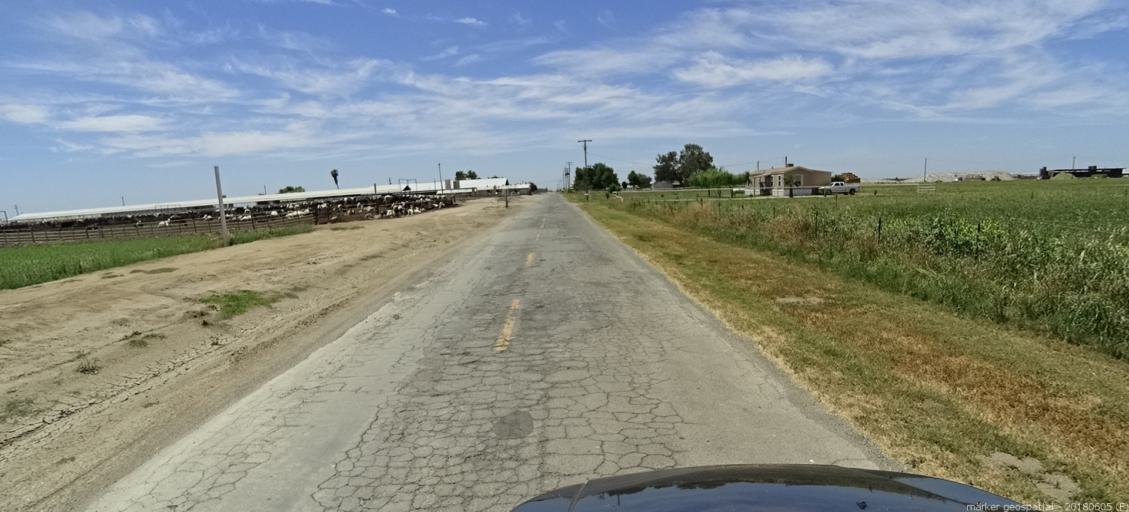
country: US
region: California
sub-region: Madera County
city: Chowchilla
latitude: 37.0907
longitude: -120.3255
